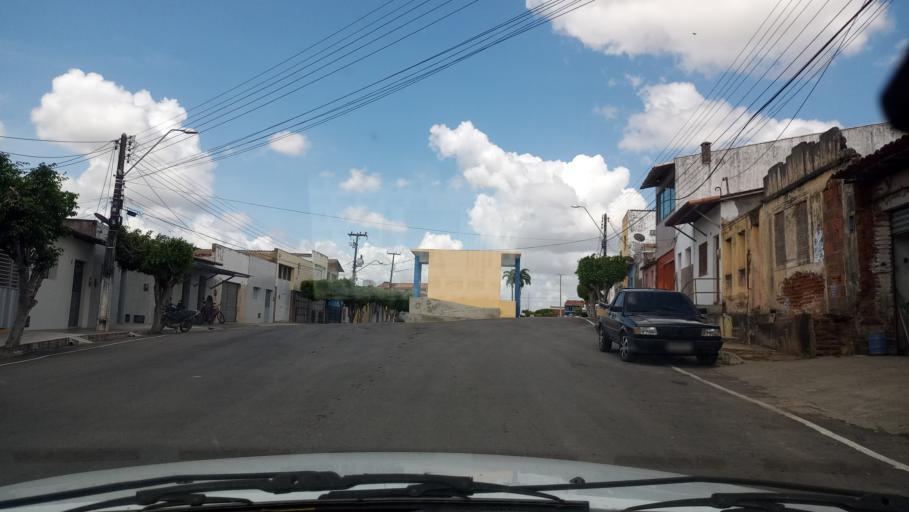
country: BR
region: Rio Grande do Norte
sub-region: Santo Antonio
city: Santo Antonio
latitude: -6.3489
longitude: -35.3743
